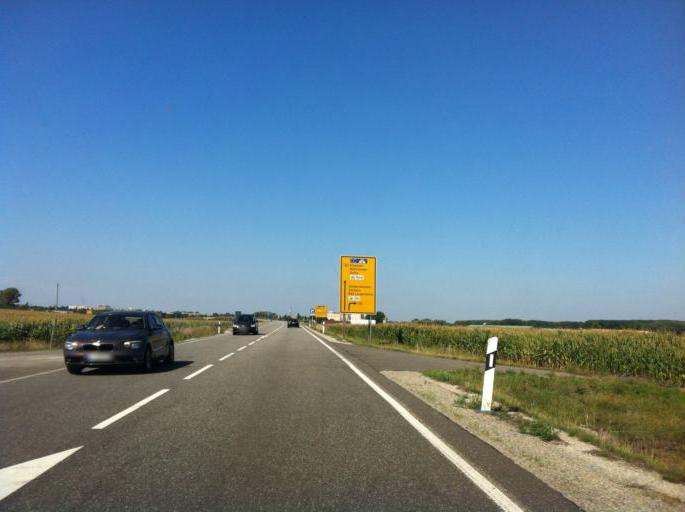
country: DE
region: Thuringia
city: Bad Langensalza
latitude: 51.0997
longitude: 10.6822
